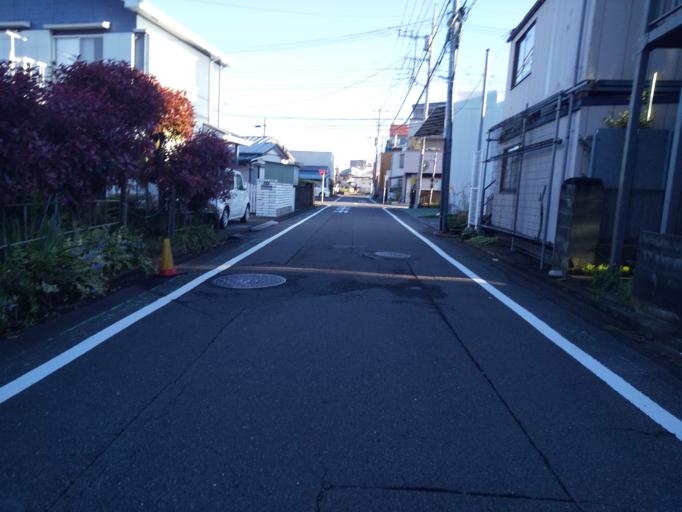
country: JP
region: Kanagawa
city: Zama
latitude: 35.5625
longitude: 139.3744
